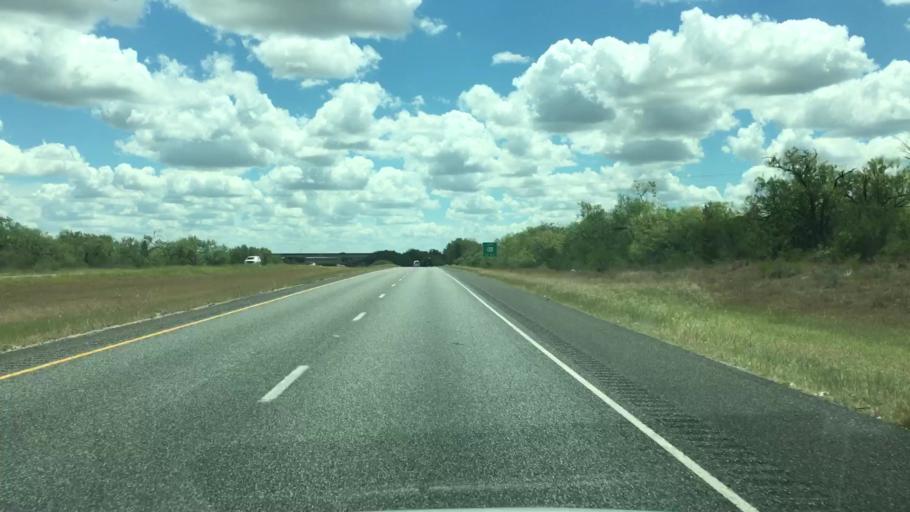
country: US
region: Texas
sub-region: Atascosa County
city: Pleasanton
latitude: 28.9149
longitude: -98.4349
